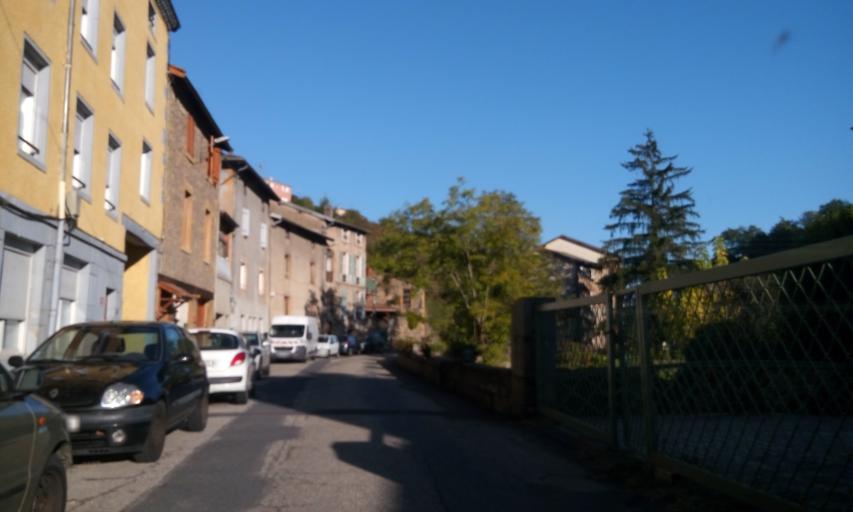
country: FR
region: Rhone-Alpes
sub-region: Departement du Rhone
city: Tarare
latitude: 45.9240
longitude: 4.4562
